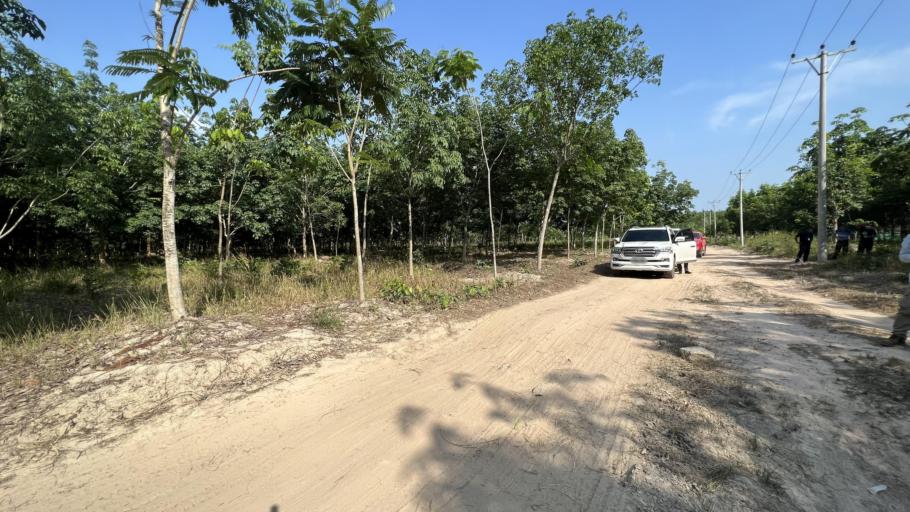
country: MM
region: Yangon
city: Twante
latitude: 16.6762
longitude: 95.9588
